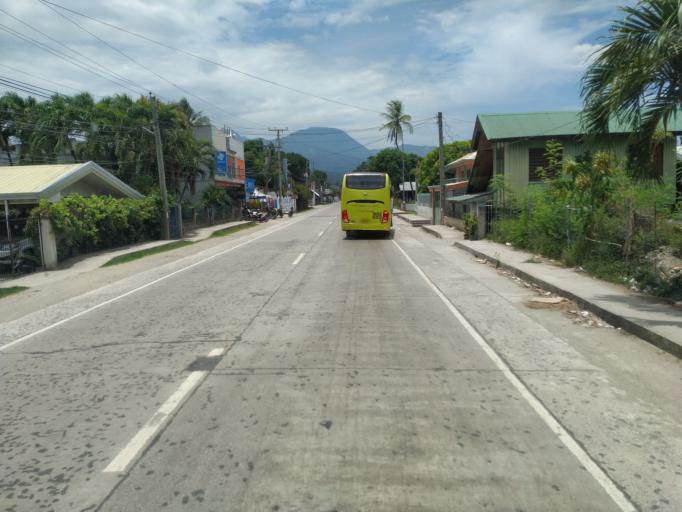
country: PH
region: Central Visayas
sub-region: Province of Negros Oriental
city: Sibulan
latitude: 9.3598
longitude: 123.2834
